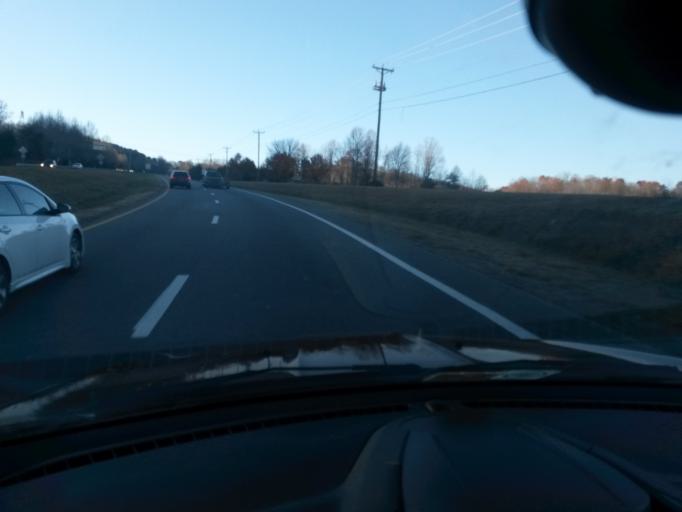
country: US
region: Virginia
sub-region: Henry County
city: Stanleytown
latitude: 36.8401
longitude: -79.9184
